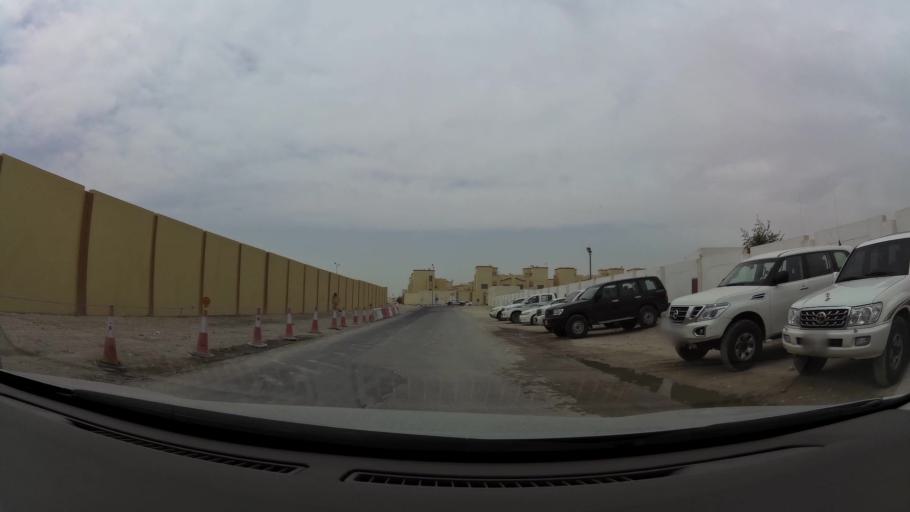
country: QA
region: Baladiyat ar Rayyan
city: Ar Rayyan
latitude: 25.2295
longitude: 51.4491
